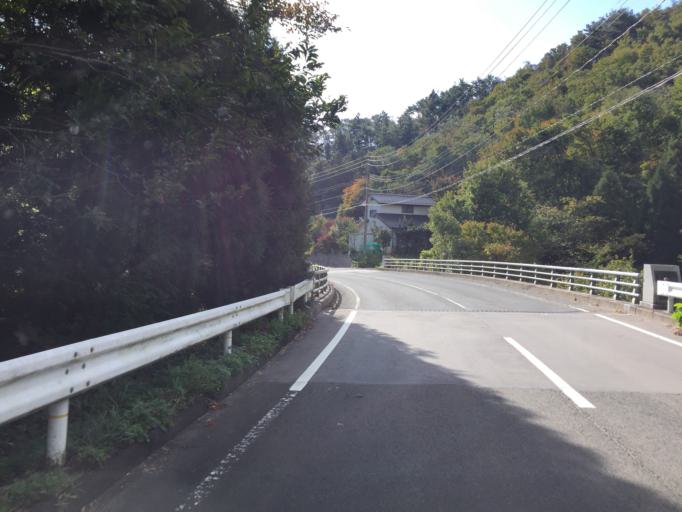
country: JP
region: Fukushima
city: Fukushima-shi
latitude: 37.7974
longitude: 140.3885
